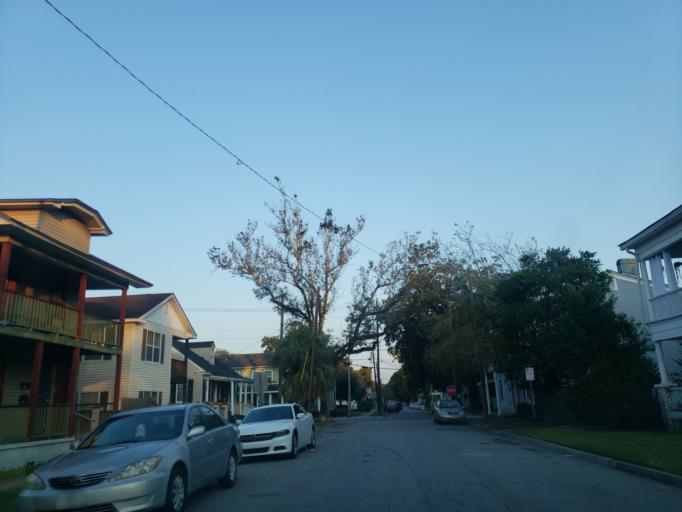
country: US
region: Georgia
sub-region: Chatham County
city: Savannah
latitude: 32.0623
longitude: -81.0809
